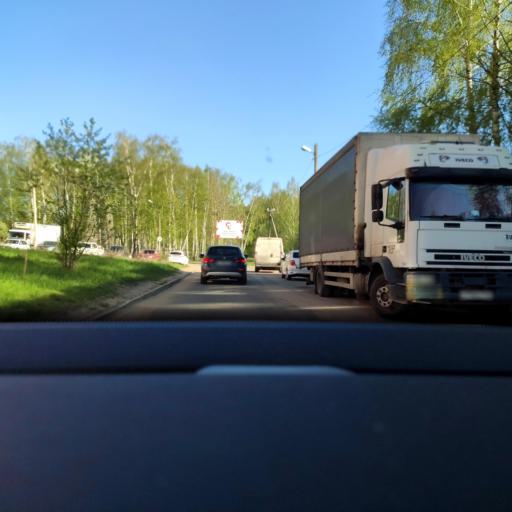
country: RU
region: Moskovskaya
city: Dmitrov
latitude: 56.3580
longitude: 37.5649
